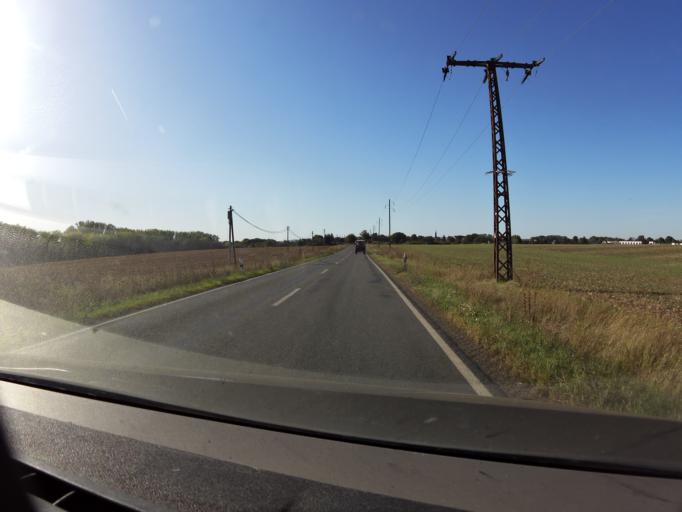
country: DE
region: Saxony-Anhalt
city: Wegeleben
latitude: 51.8880
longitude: 11.1958
